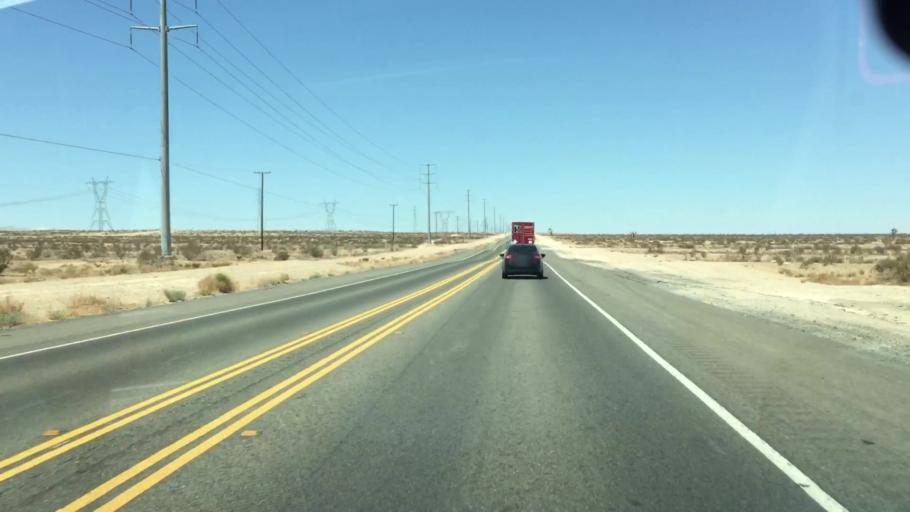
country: US
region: California
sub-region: San Bernardino County
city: Adelanto
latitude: 34.6619
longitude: -117.4403
